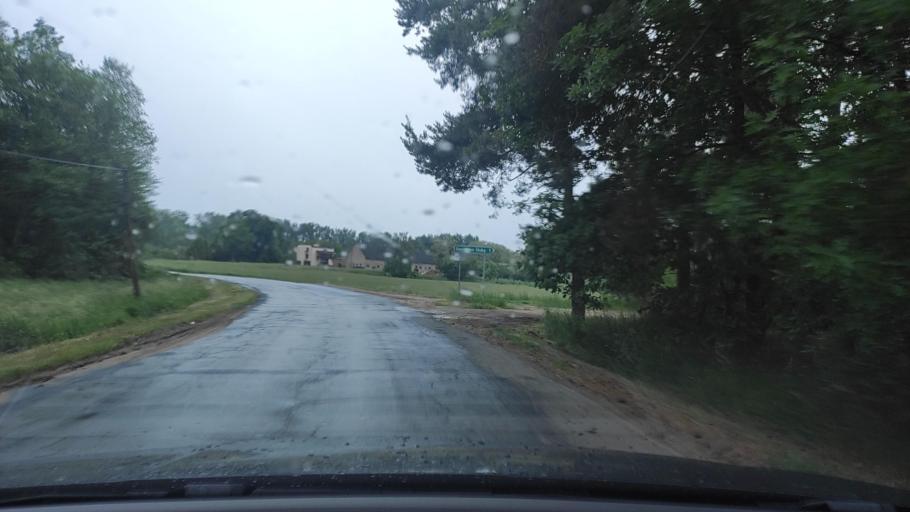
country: PL
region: Greater Poland Voivodeship
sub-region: Powiat poznanski
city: Kobylnica
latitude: 52.4518
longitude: 17.1606
